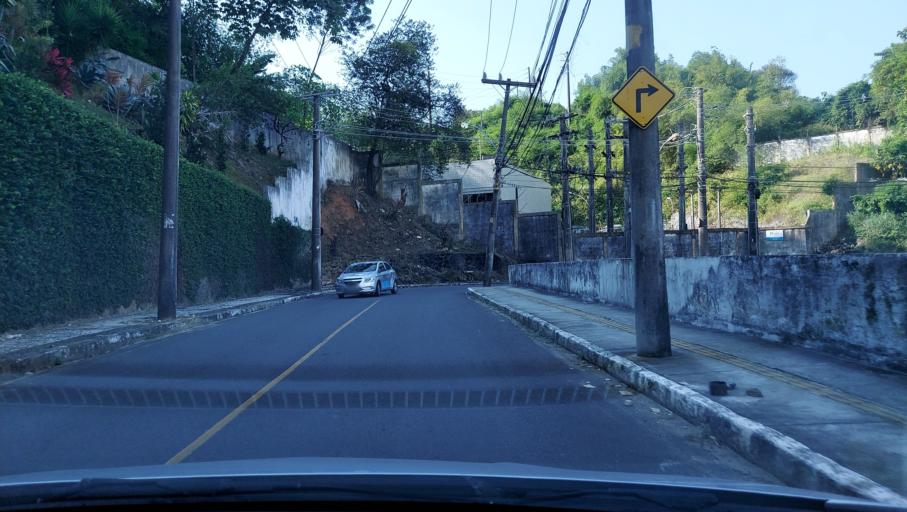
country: BR
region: Bahia
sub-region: Salvador
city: Salvador
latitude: -12.9840
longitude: -38.4696
